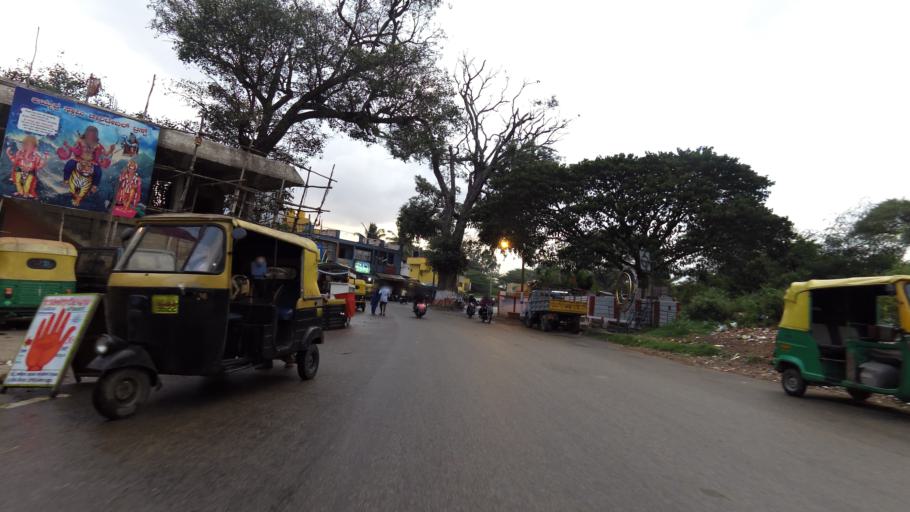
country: IN
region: Karnataka
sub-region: Bangalore Urban
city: Bangalore
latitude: 12.9948
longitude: 77.6439
